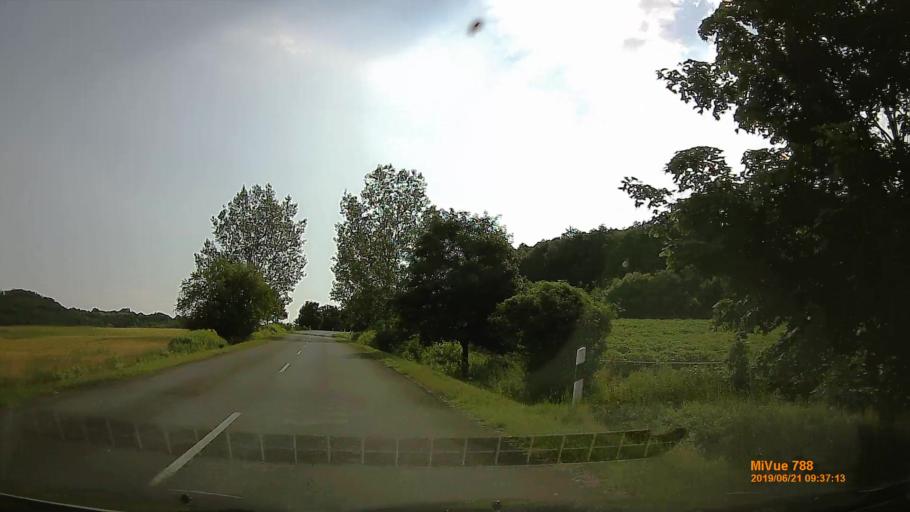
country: HU
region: Somogy
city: Taszar
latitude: 46.3146
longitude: 17.9135
